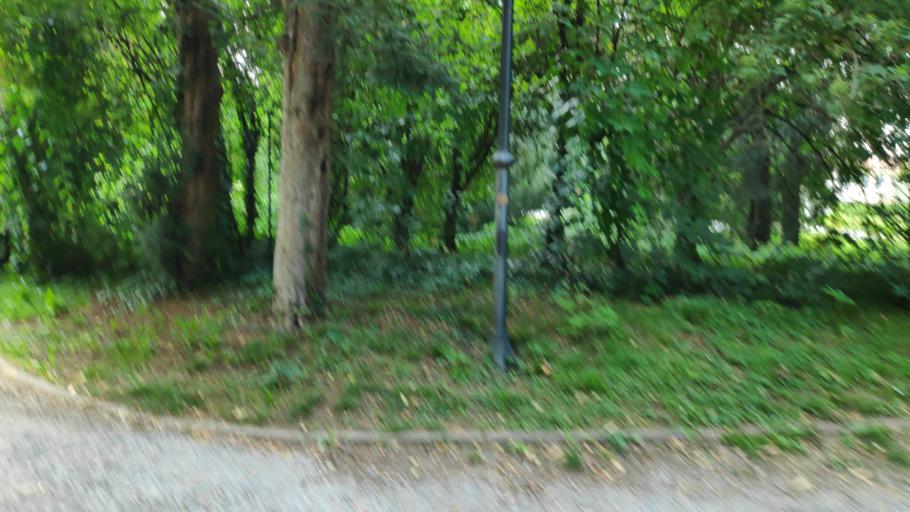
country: IT
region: Lombardy
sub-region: Citta metropolitana di Milano
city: Cernusco sul Naviglio
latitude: 45.5220
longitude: 9.3354
